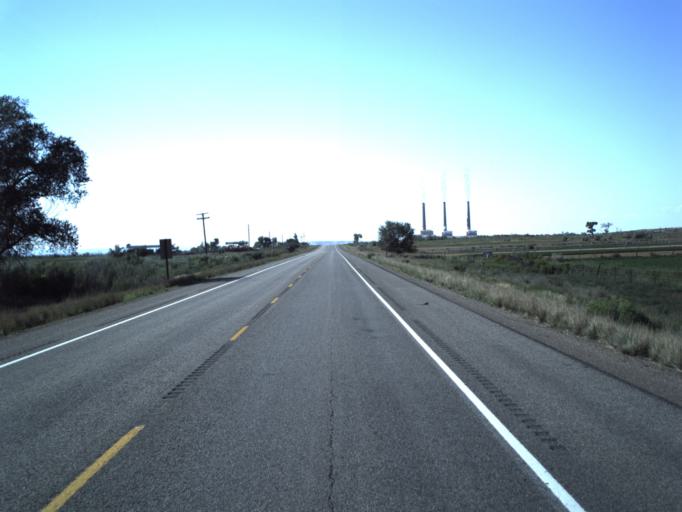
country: US
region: Utah
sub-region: Emery County
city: Castle Dale
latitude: 39.2053
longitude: -111.0243
